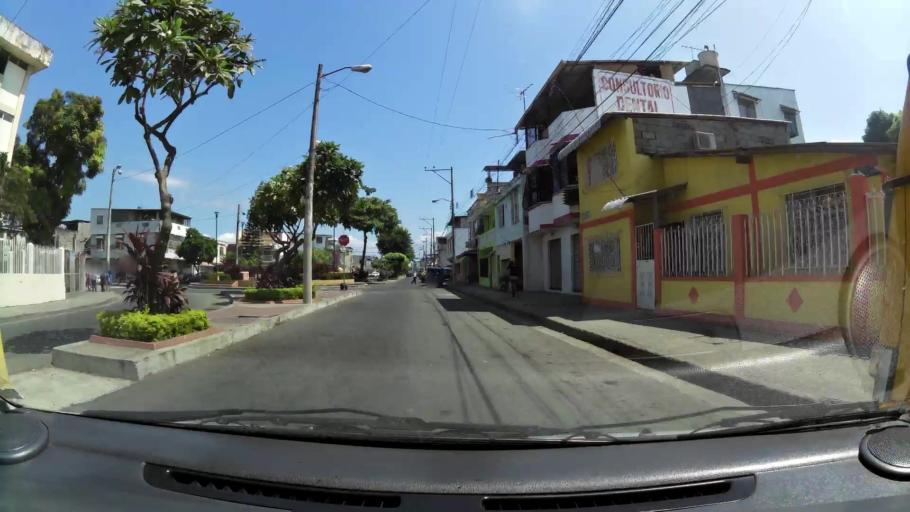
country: EC
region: Guayas
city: Guayaquil
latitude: -2.2324
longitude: -79.9034
